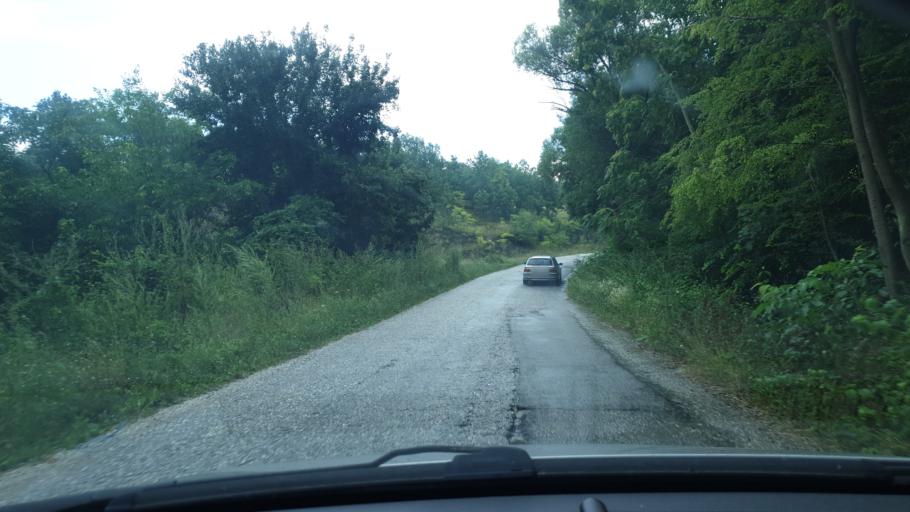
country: RS
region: Central Serbia
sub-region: Sumadijski Okrug
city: Kragujevac
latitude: 44.0699
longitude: 20.7889
